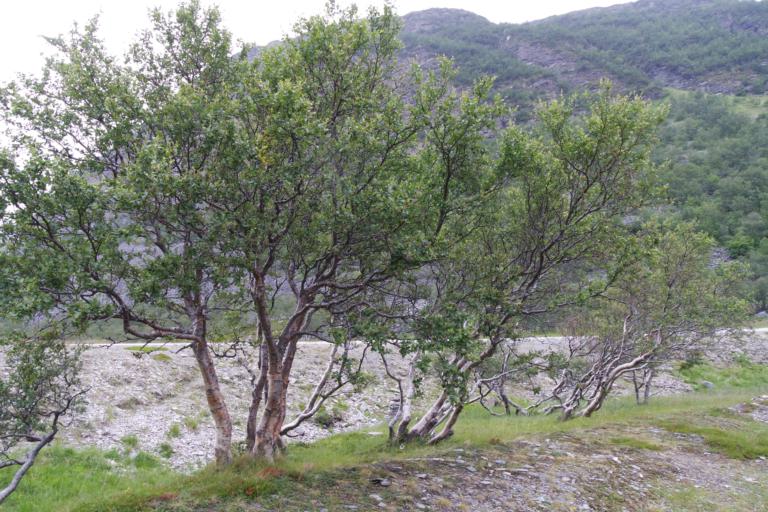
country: NO
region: Finnmark Fylke
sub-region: Porsanger
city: Lakselv
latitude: 70.6279
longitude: 25.3334
